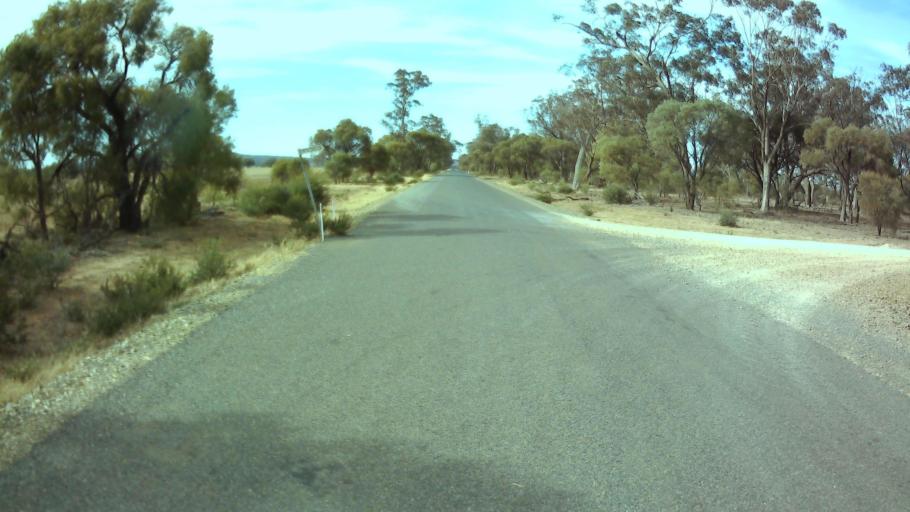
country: AU
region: New South Wales
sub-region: Weddin
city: Grenfell
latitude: -33.8717
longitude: 147.8579
